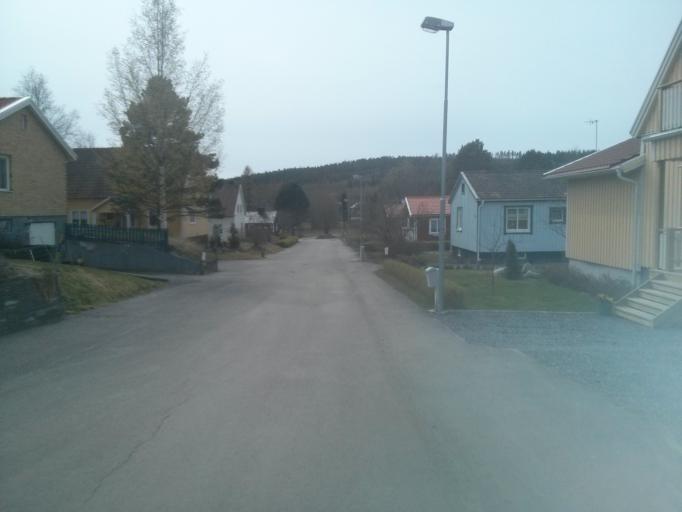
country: SE
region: Vaesternorrland
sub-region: Haernoesands Kommun
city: Haernoesand
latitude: 62.6340
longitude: 17.9092
